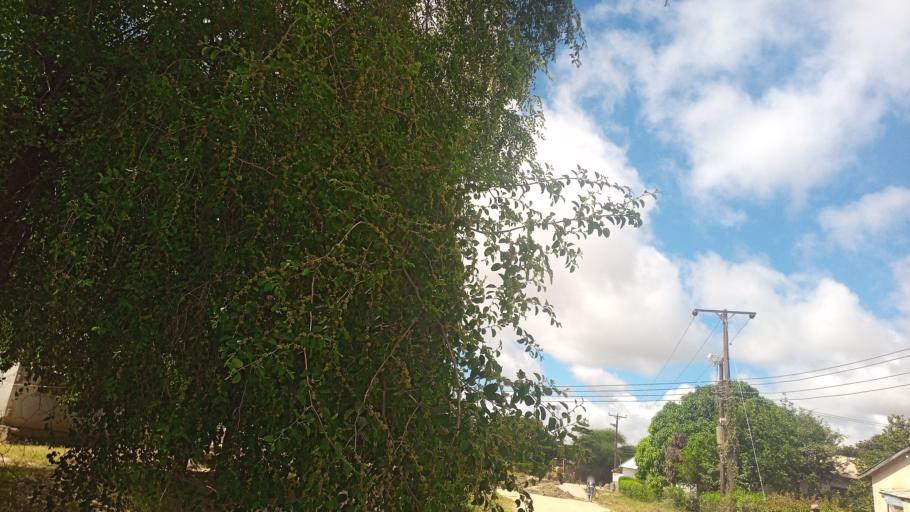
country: TZ
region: Dodoma
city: Dodoma
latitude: -6.1916
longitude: 35.7348
